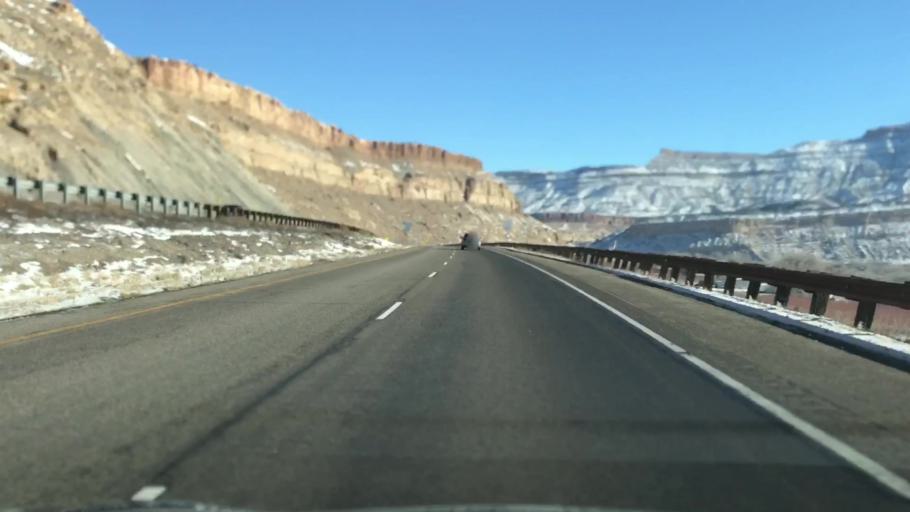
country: US
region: Colorado
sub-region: Mesa County
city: Palisade
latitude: 39.1169
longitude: -108.3488
